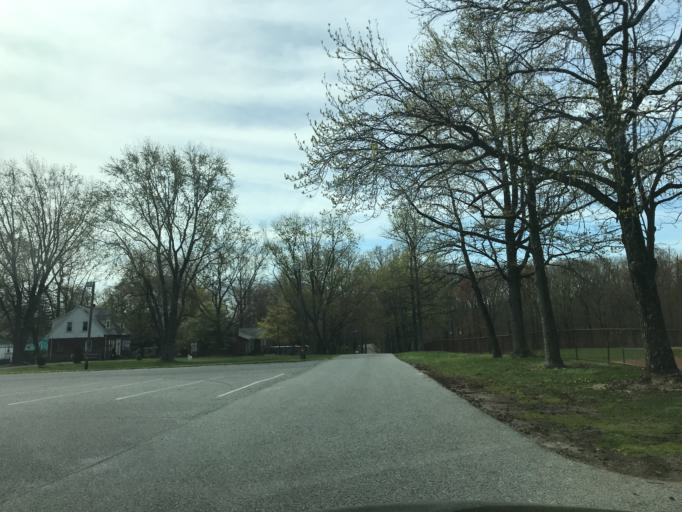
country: US
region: Maryland
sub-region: Baltimore County
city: Middle River
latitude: 39.3065
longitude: -76.4327
